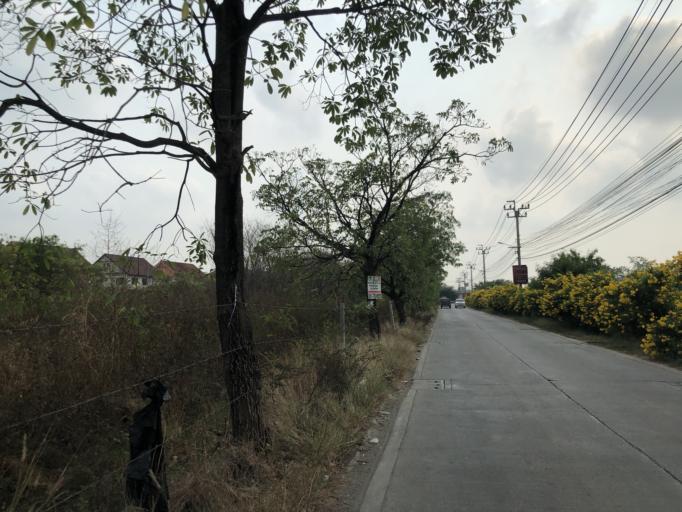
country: TH
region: Bangkok
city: Bang Na
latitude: 13.5861
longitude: 100.7015
